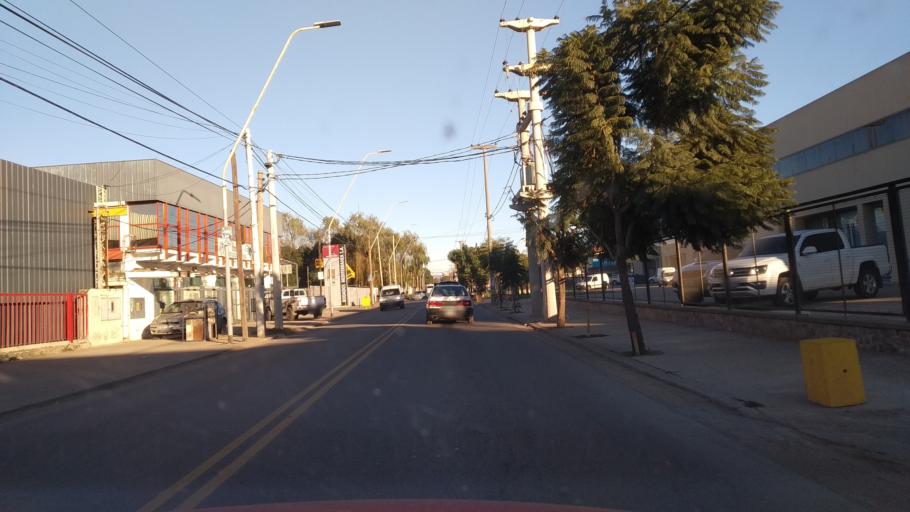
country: AR
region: Cordoba
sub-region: Departamento de Capital
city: Cordoba
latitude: -31.3432
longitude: -64.2115
